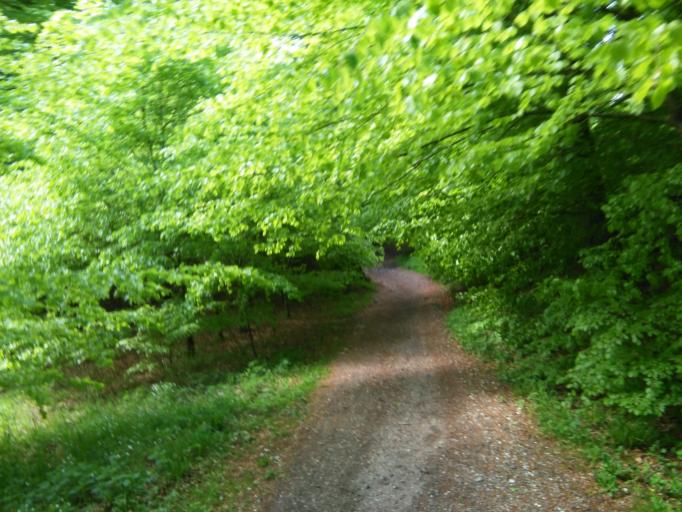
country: DK
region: Central Jutland
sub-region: Arhus Kommune
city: Beder
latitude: 56.0958
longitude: 10.2372
